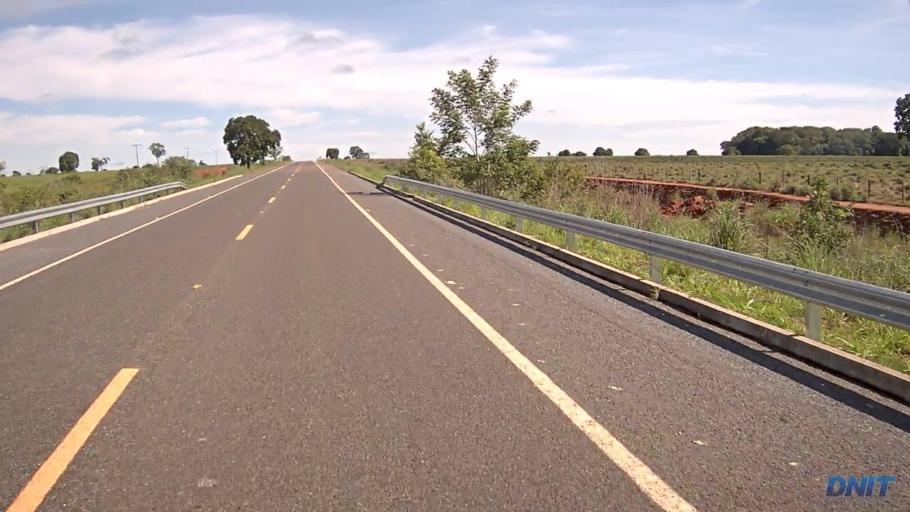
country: BR
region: Goias
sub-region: Sao Miguel Do Araguaia
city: Sao Miguel do Araguaia
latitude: -13.3776
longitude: -50.1417
